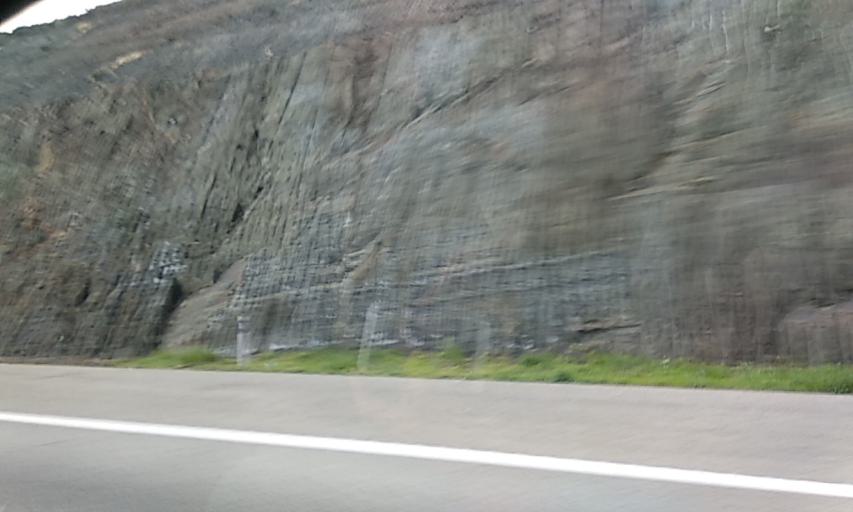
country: PT
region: Porto
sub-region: Trofa
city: Bougado
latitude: 41.3227
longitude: -8.5176
